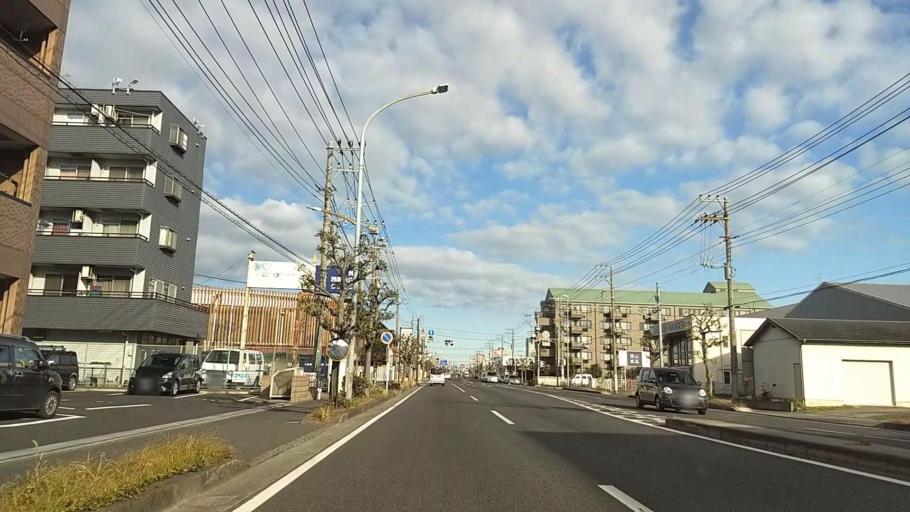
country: JP
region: Kanagawa
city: Hiratsuka
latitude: 35.3425
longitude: 139.3562
